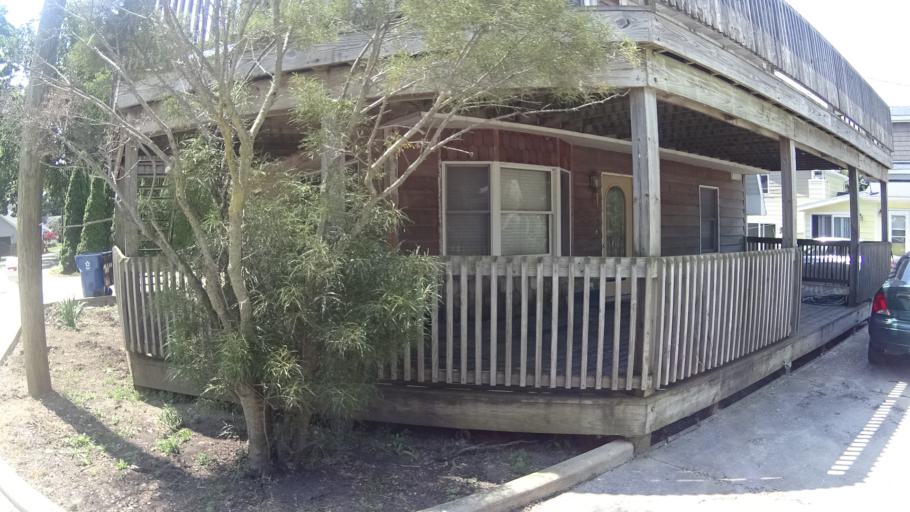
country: US
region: Ohio
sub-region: Erie County
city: Huron
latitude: 41.4128
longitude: -82.5871
